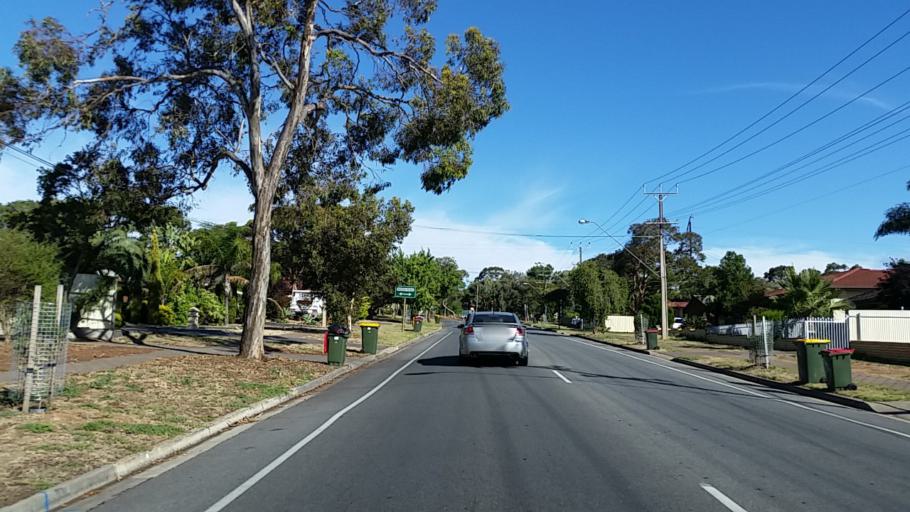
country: AU
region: South Australia
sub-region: Salisbury
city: Salisbury
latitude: -34.7887
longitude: 138.6633
